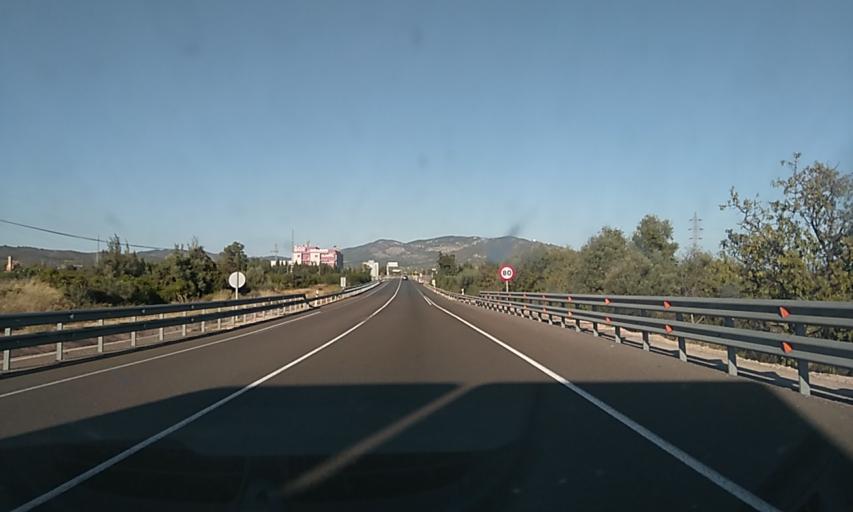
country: ES
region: Valencia
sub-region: Provincia de Castello
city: Torreblanca
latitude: 40.2307
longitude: 0.2178
